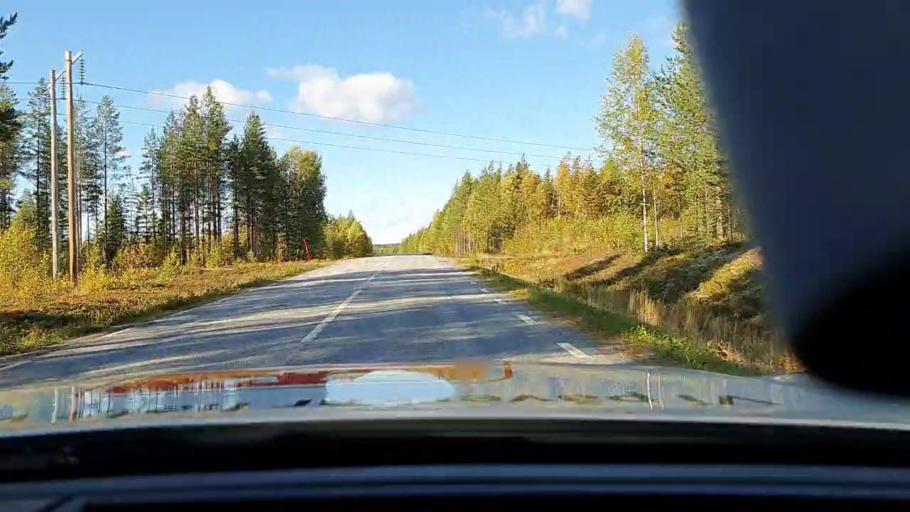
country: SE
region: Norrbotten
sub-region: Pitea Kommun
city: Norrfjarden
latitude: 65.4533
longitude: 21.4563
